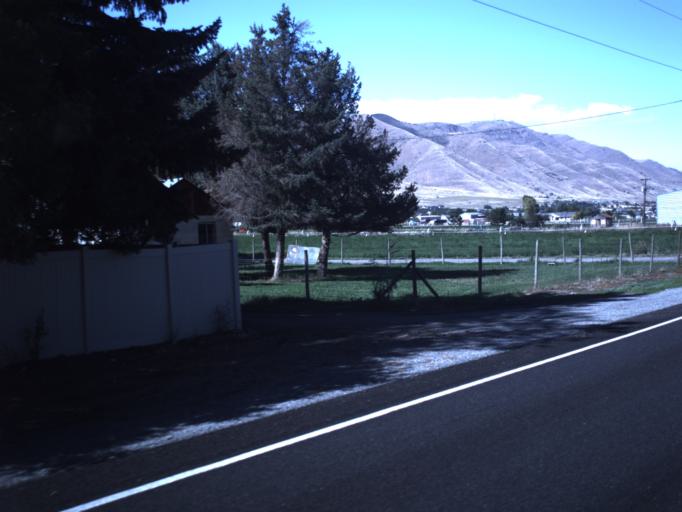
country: US
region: Utah
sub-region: Utah County
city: West Mountain
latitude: 40.0376
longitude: -111.7872
